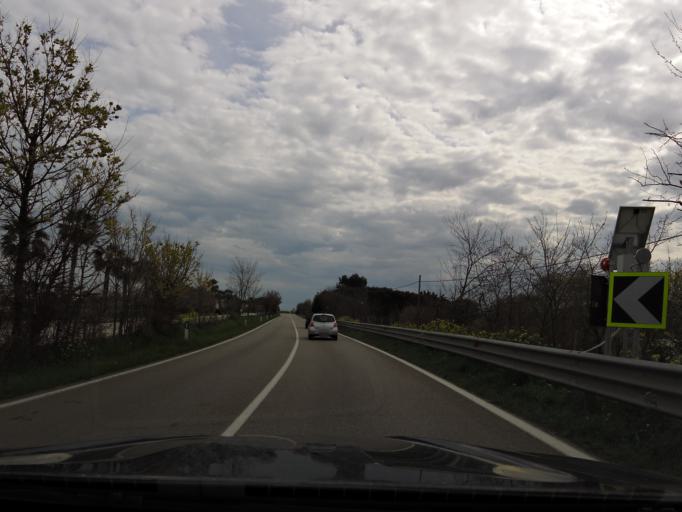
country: IT
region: The Marches
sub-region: Provincia di Macerata
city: Porto Potenza Picena
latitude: 43.3941
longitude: 13.6798
